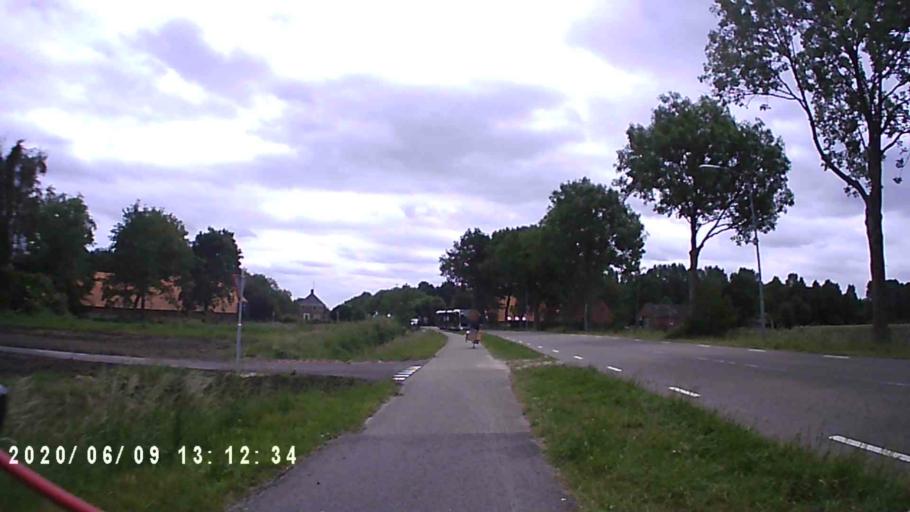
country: NL
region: Groningen
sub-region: Gemeente Haren
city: Haren
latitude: 53.2104
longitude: 6.6651
